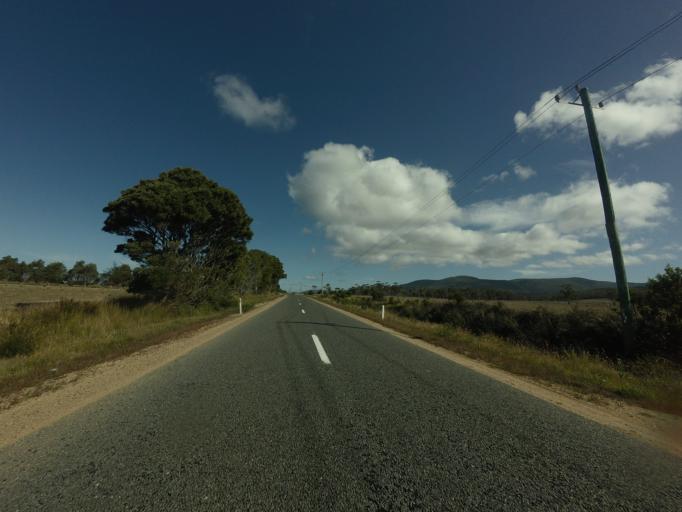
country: AU
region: Tasmania
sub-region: Break O'Day
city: St Helens
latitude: -41.7607
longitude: 148.2729
